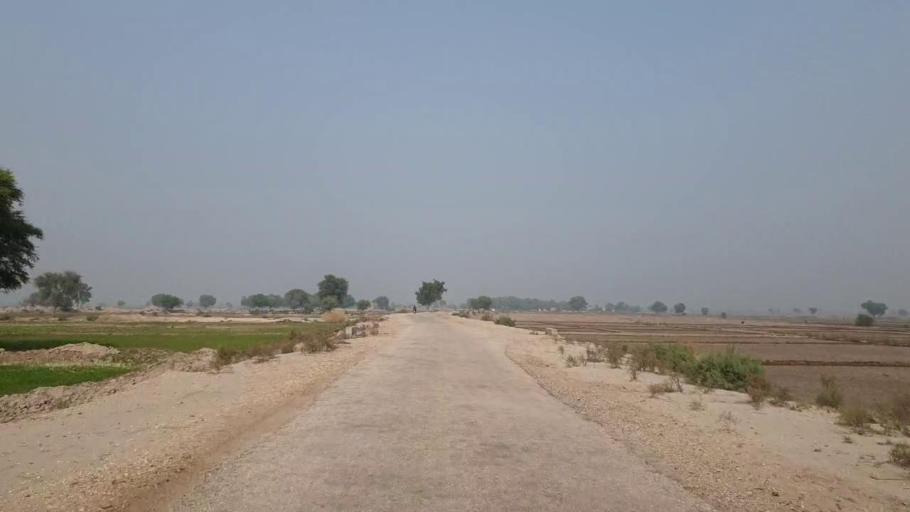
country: PK
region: Sindh
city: Bhan
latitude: 26.5175
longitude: 67.6897
